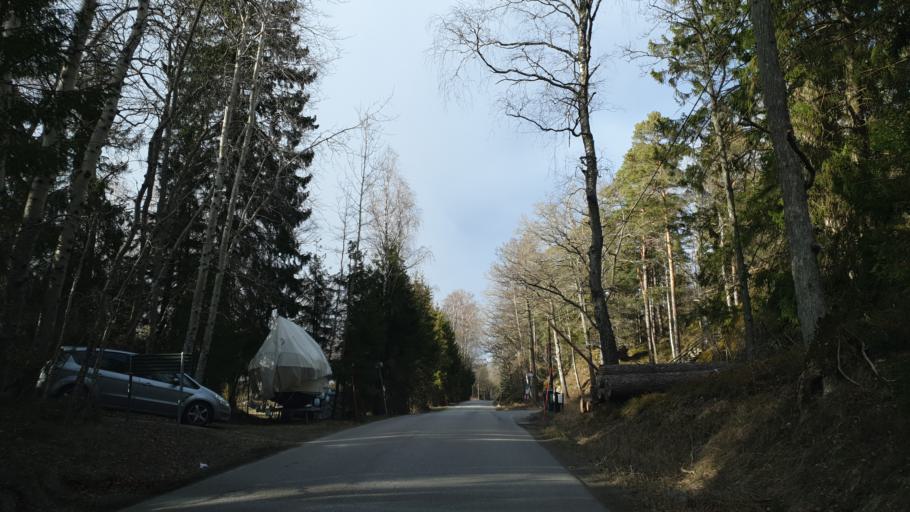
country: SE
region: Stockholm
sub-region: Varmdo Kommun
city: Holo
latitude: 59.3605
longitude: 18.6703
